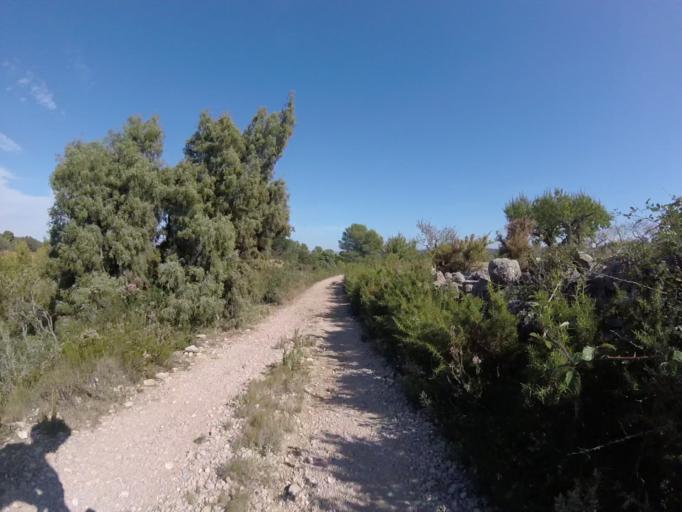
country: ES
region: Valencia
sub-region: Provincia de Castello
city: Sarratella
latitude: 40.2806
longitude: 0.0690
